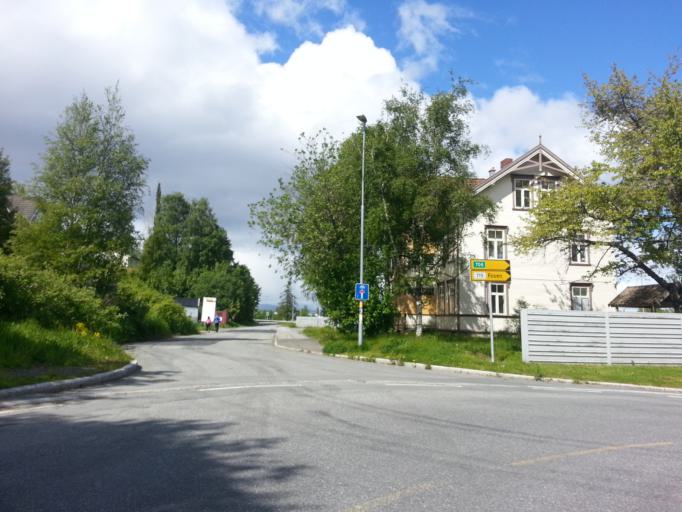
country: NO
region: Sor-Trondelag
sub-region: Trondheim
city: Trondheim
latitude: 63.4140
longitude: 10.3818
